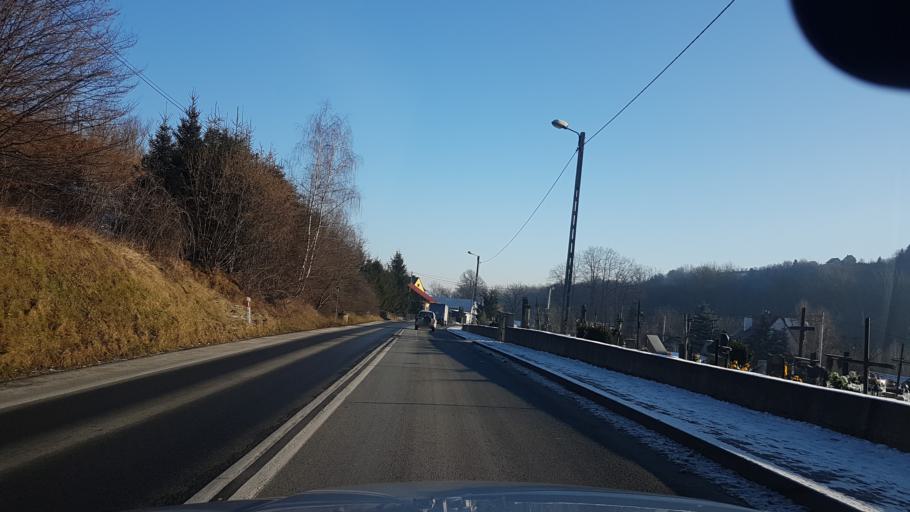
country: PL
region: Lesser Poland Voivodeship
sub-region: Powiat nowosadecki
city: Olszana
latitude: 49.5281
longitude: 20.5110
